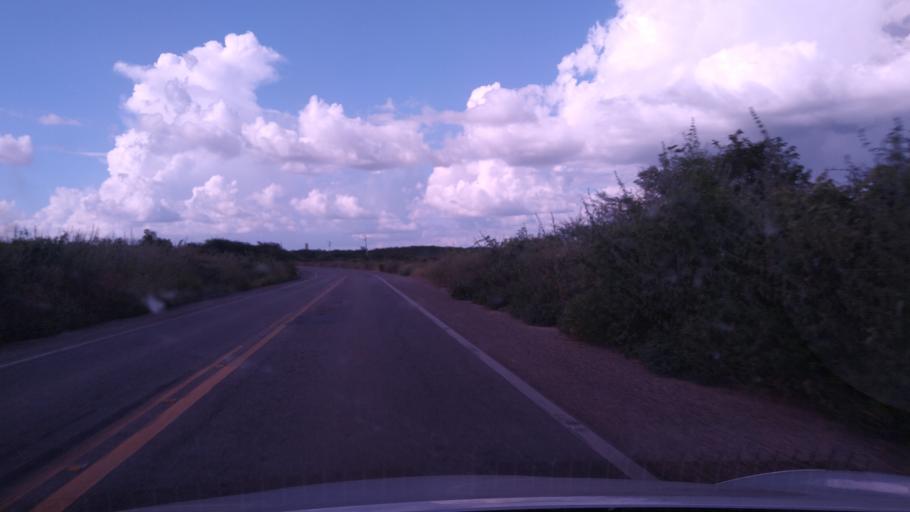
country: BR
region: Ceara
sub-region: Caninde
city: Caninde
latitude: -4.3960
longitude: -39.3156
